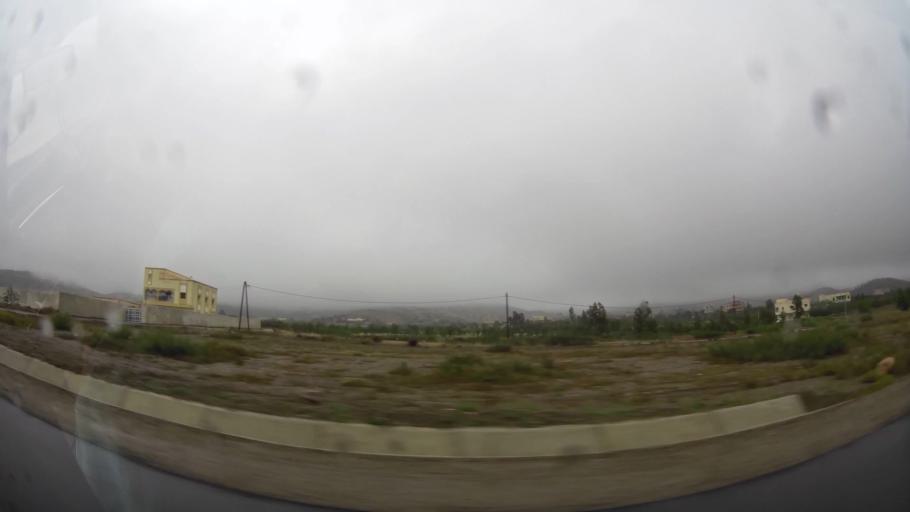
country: MA
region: Oriental
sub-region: Nador
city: Midar
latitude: 34.8409
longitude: -3.7209
